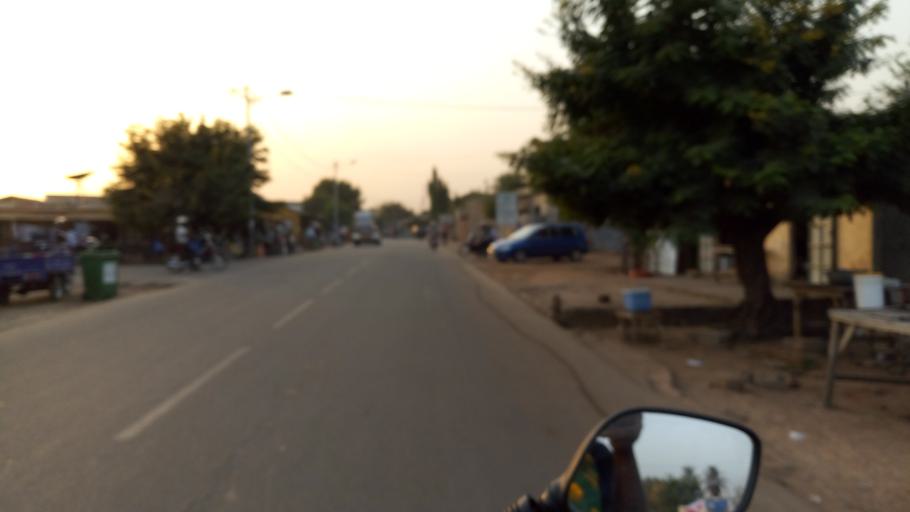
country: TG
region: Kara
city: Kara
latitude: 9.5487
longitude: 1.1944
